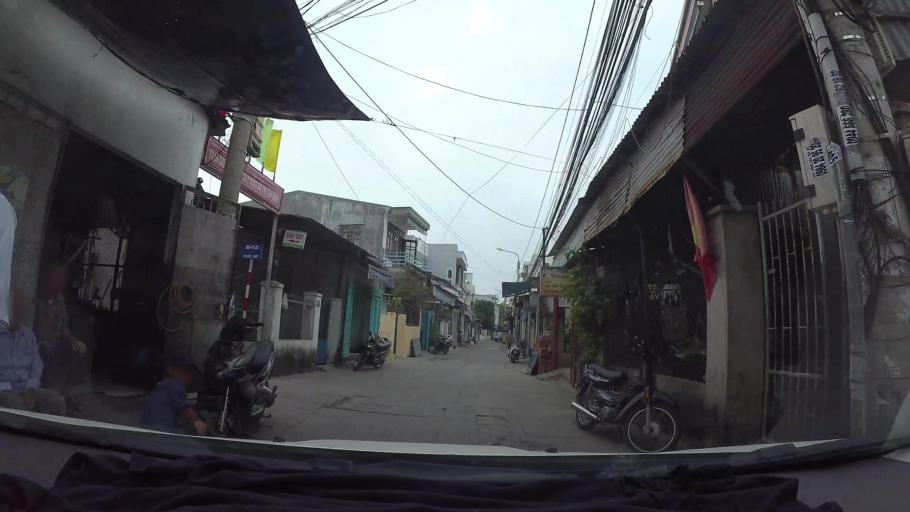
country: VN
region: Da Nang
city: Thanh Khe
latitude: 16.0627
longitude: 108.1870
